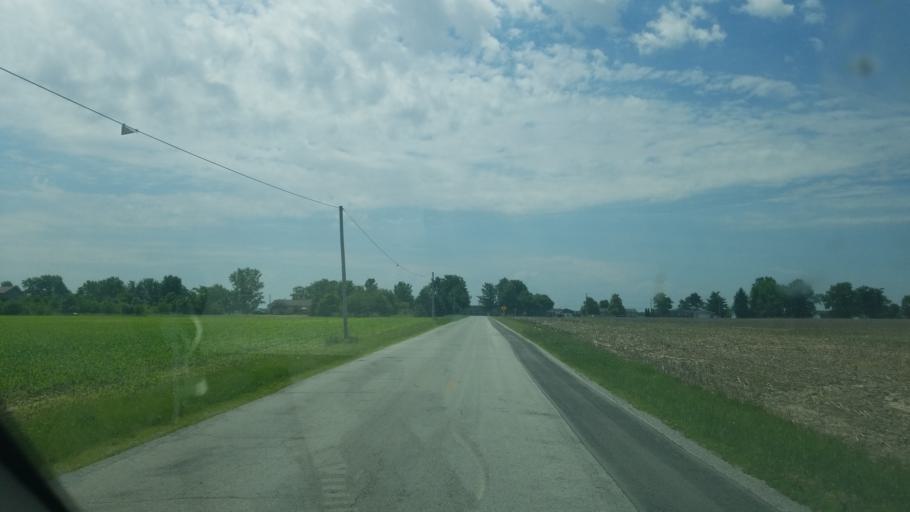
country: US
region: Ohio
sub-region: Wood County
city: North Baltimore
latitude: 41.2563
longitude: -83.5930
